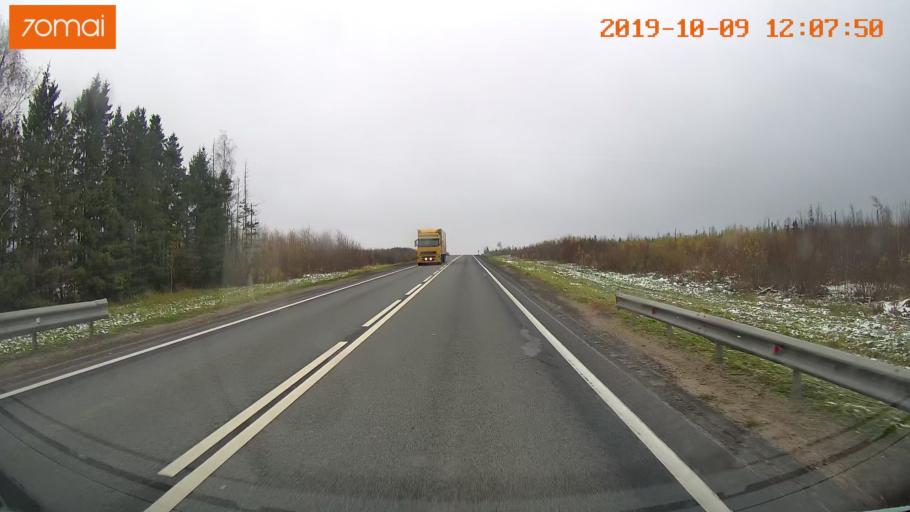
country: RU
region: Jaroslavl
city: Prechistoye
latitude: 58.5946
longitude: 40.3440
